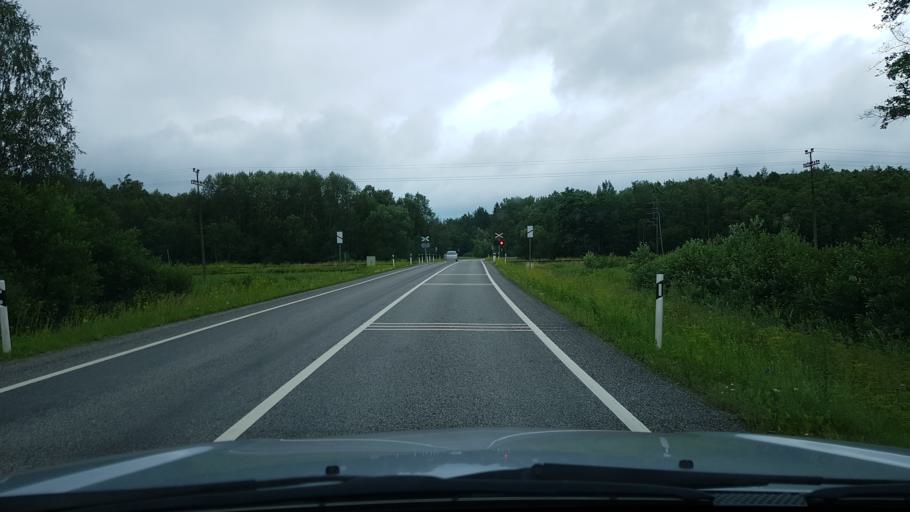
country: EE
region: Ida-Virumaa
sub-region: Narva-Joesuu linn
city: Narva-Joesuu
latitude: 59.3646
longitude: 27.9325
